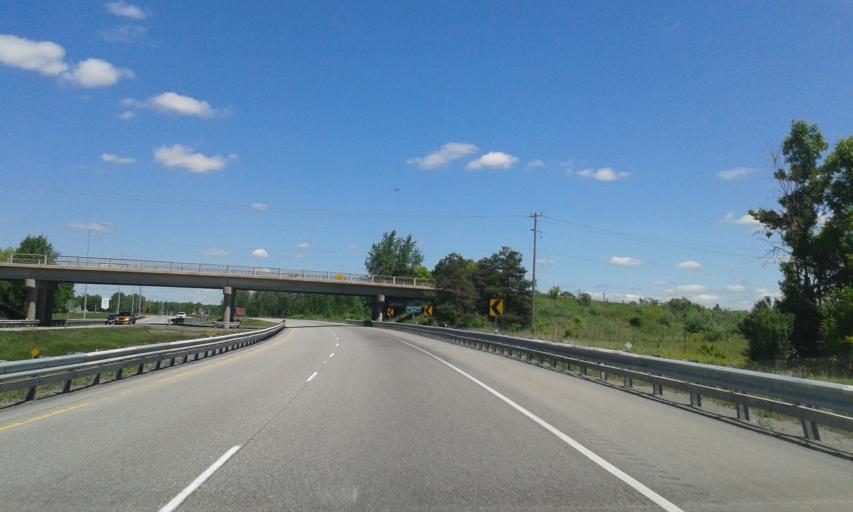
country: US
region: New York
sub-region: St. Lawrence County
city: Norfolk
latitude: 44.9659
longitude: -75.0814
